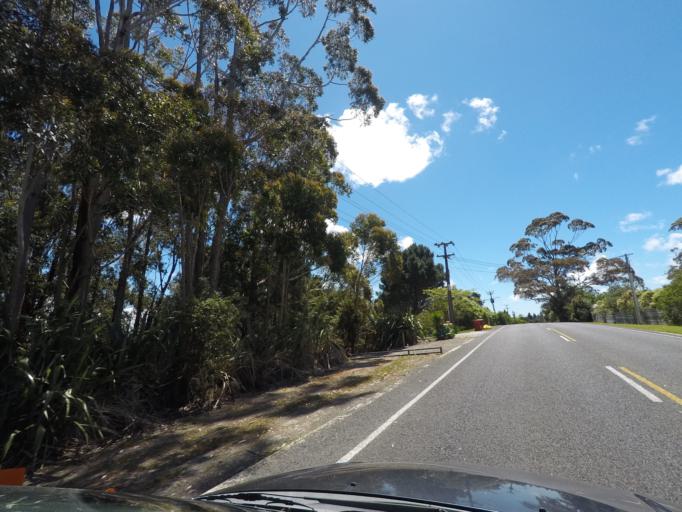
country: NZ
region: Auckland
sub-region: Auckland
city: Rothesay Bay
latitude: -36.7535
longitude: 174.6651
